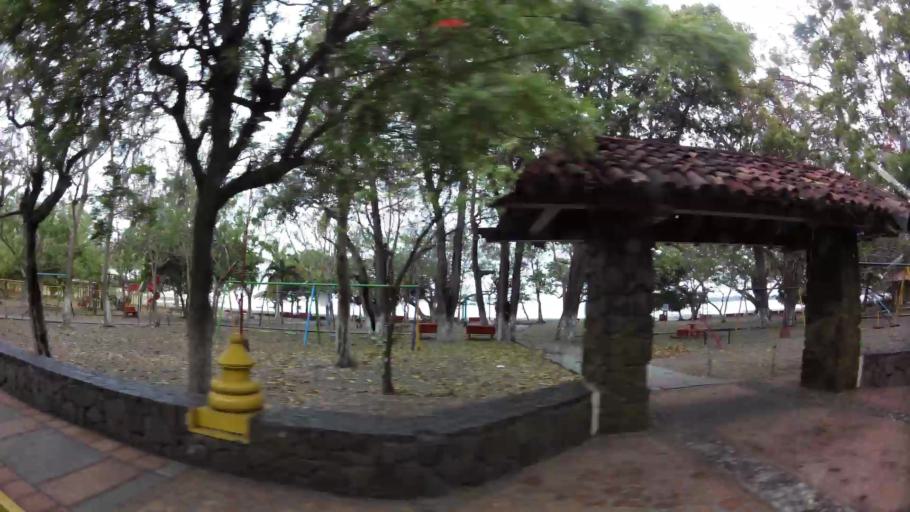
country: NI
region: Granada
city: Granada
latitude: 11.9231
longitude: -85.9404
